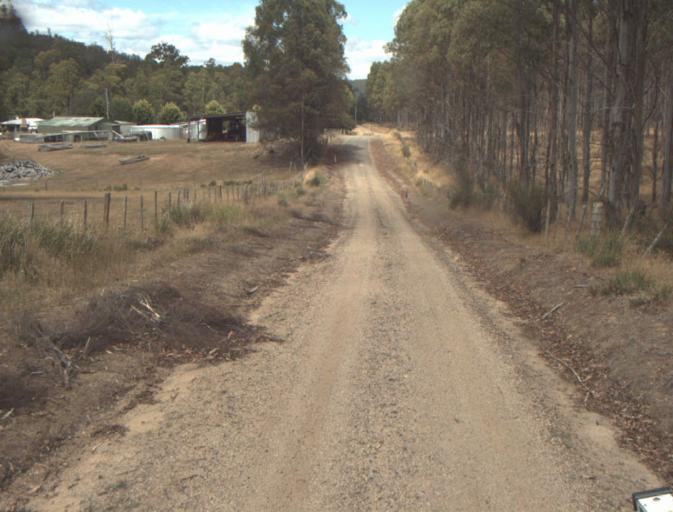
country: AU
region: Tasmania
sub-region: Dorset
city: Scottsdale
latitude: -41.4136
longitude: 147.5257
